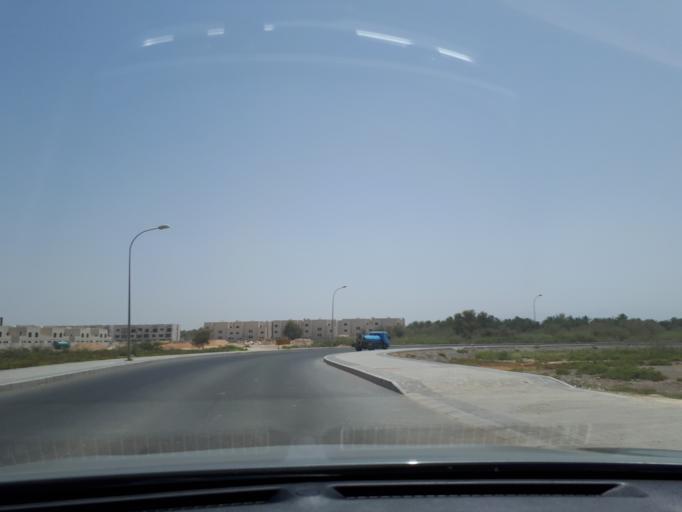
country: OM
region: Muhafazat Masqat
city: As Sib al Jadidah
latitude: 23.6827
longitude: 58.1477
